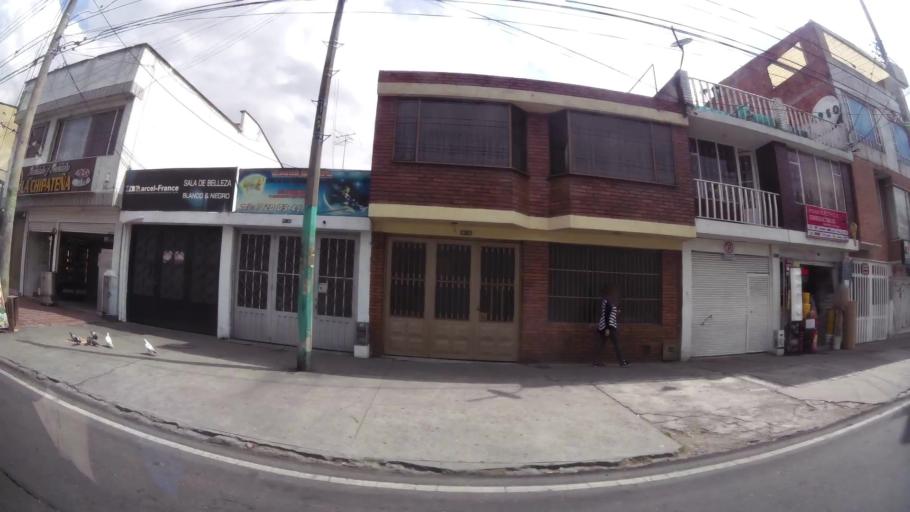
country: CO
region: Bogota D.C.
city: Bogota
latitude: 4.6067
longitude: -74.1165
